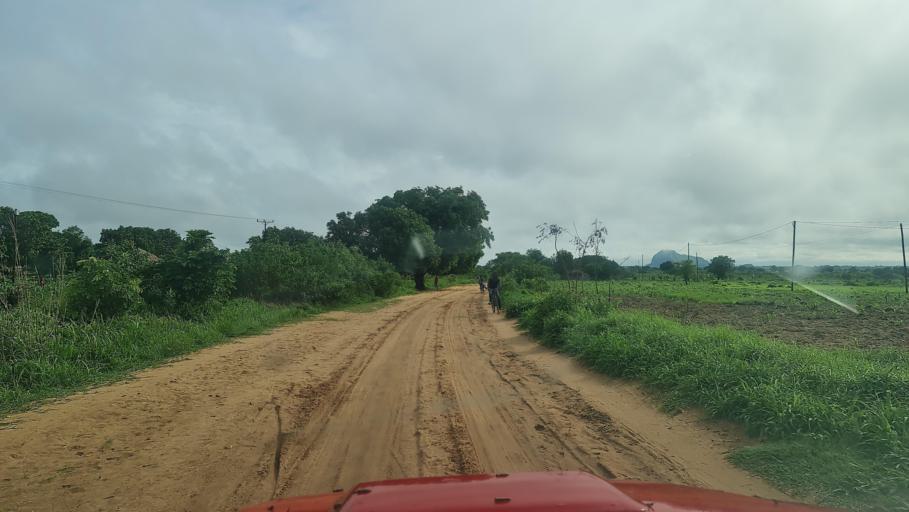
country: MW
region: Southern Region
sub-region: Nsanje District
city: Nsanje
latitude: -17.2949
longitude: 35.5947
